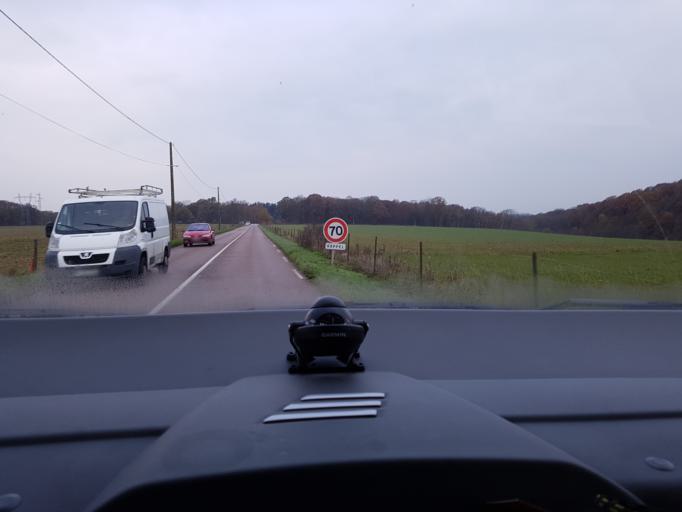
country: FR
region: Haute-Normandie
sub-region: Departement de la Seine-Maritime
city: Saint-Pierre-de-Varengeville
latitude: 49.4975
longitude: 0.9203
